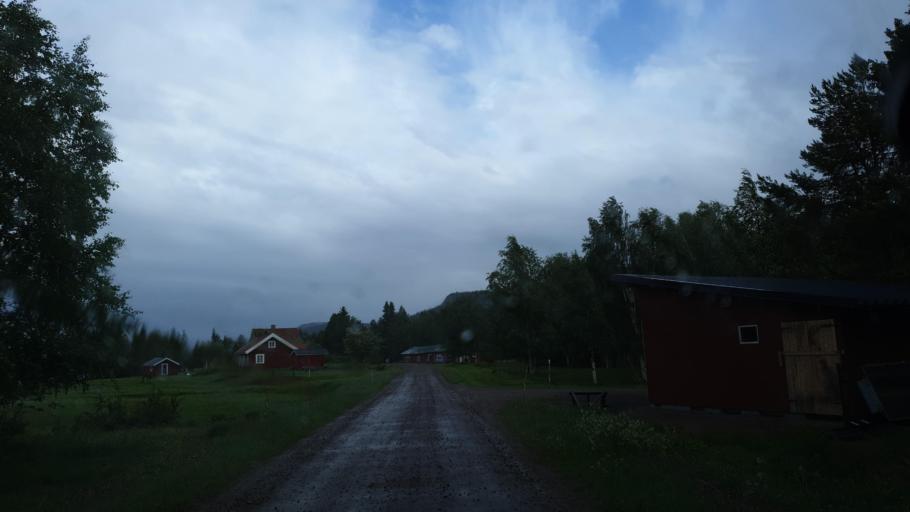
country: SE
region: Norrbotten
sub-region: Arvidsjaurs Kommun
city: Arvidsjaur
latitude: 65.7058
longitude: 18.7144
